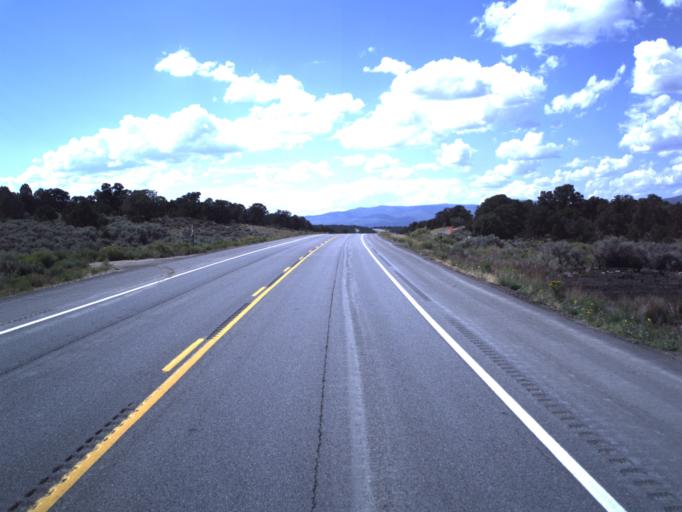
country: US
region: Utah
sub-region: Duchesne County
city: Duchesne
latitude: 40.1859
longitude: -110.6690
